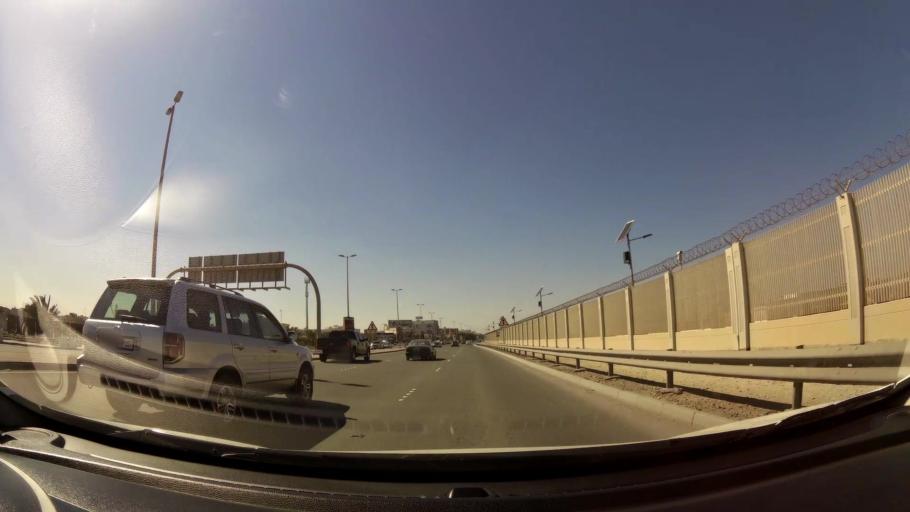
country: BH
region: Muharraq
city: Al Hadd
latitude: 26.2570
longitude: 50.6514
